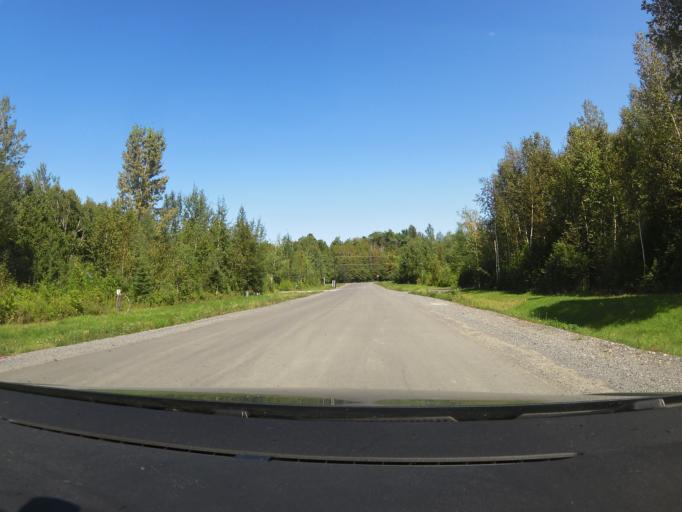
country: CA
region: Ontario
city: Bells Corners
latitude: 45.2909
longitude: -75.9954
